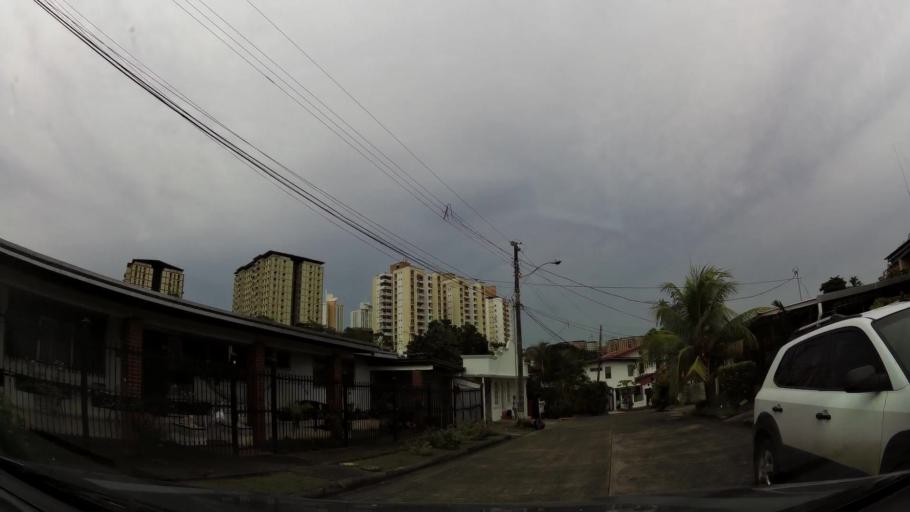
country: PA
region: Panama
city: Panama
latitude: 9.0216
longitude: -79.5239
